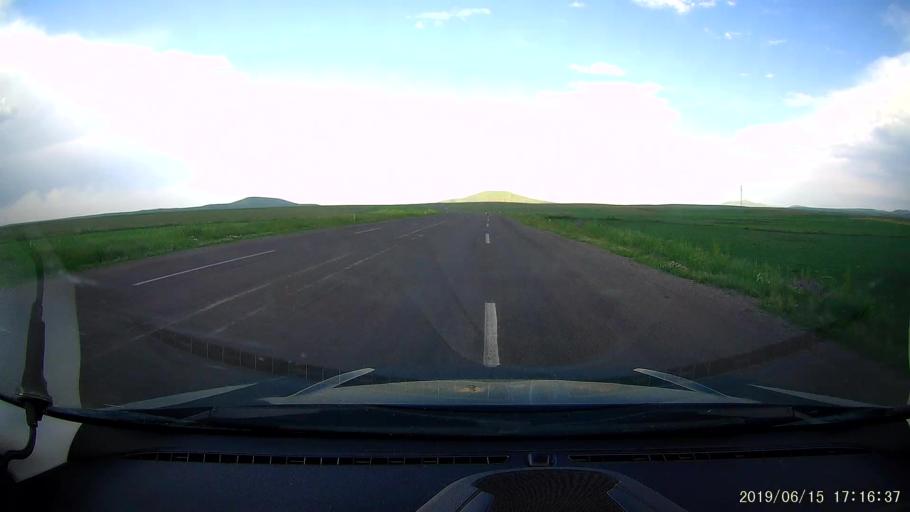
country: TR
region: Kars
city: Kars
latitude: 40.6145
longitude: 43.2212
